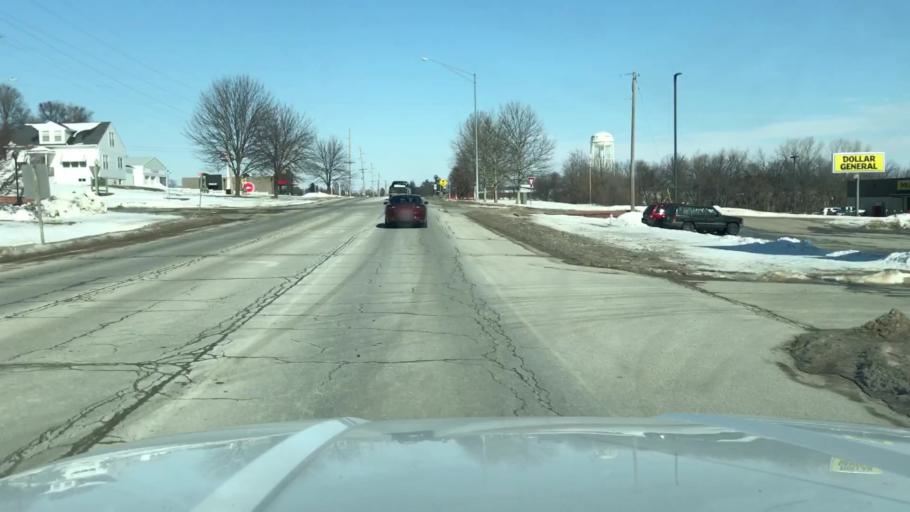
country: US
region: Missouri
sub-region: Andrew County
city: Savannah
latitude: 39.9410
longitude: -94.8219
